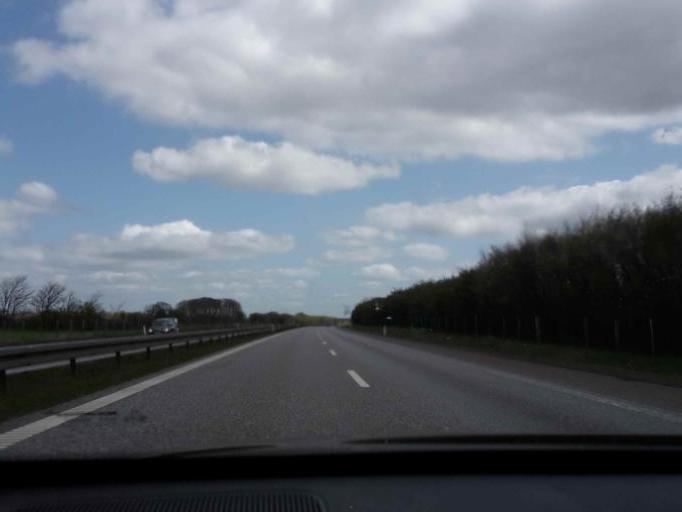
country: DK
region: South Denmark
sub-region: Esbjerg Kommune
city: Bramming
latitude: 55.5139
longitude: 8.7645
